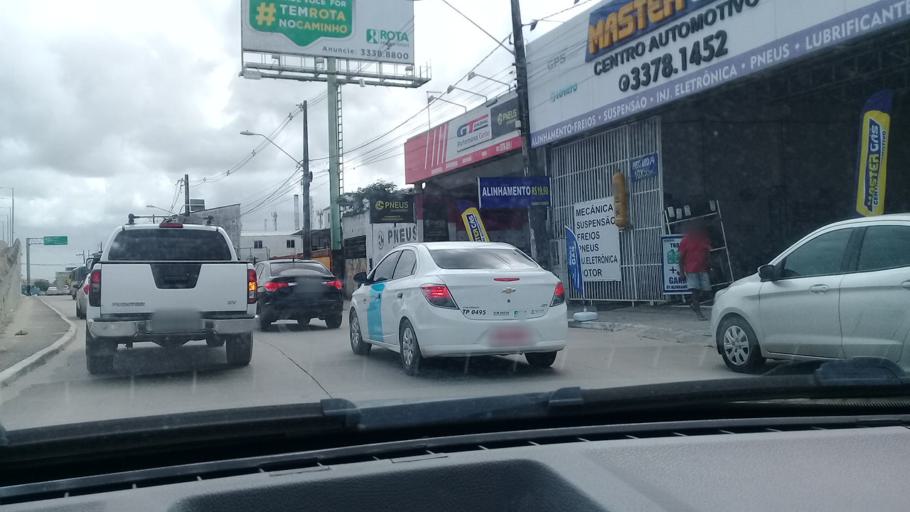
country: BR
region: Pernambuco
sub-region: Jaboatao Dos Guararapes
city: Jaboatao
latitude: -8.1575
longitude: -34.9255
